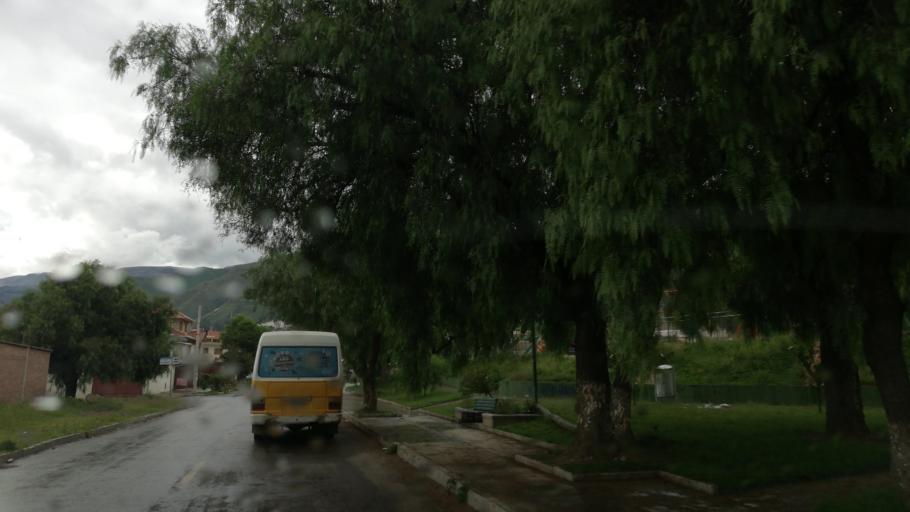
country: BO
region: Cochabamba
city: Cochabamba
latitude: -17.3494
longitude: -66.1761
